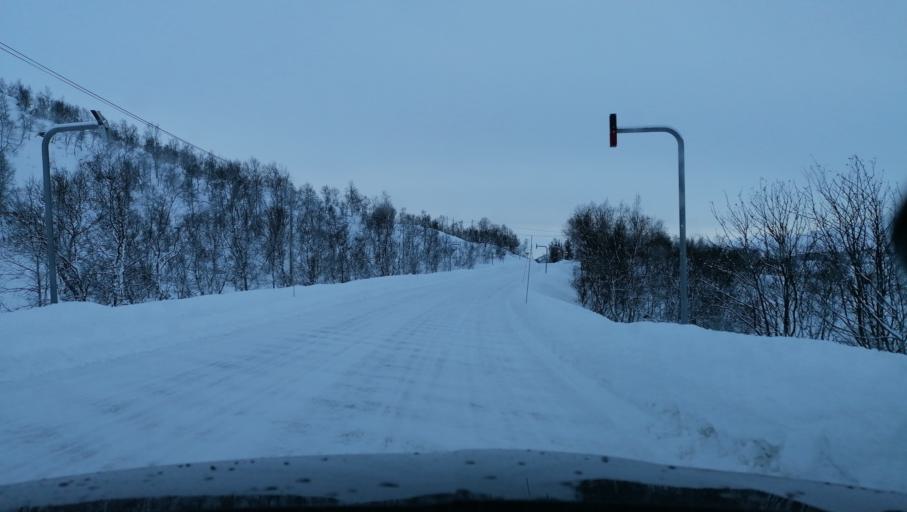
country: NO
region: Aust-Agder
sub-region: Bykle
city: Hovden
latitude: 59.6417
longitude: 7.4571
